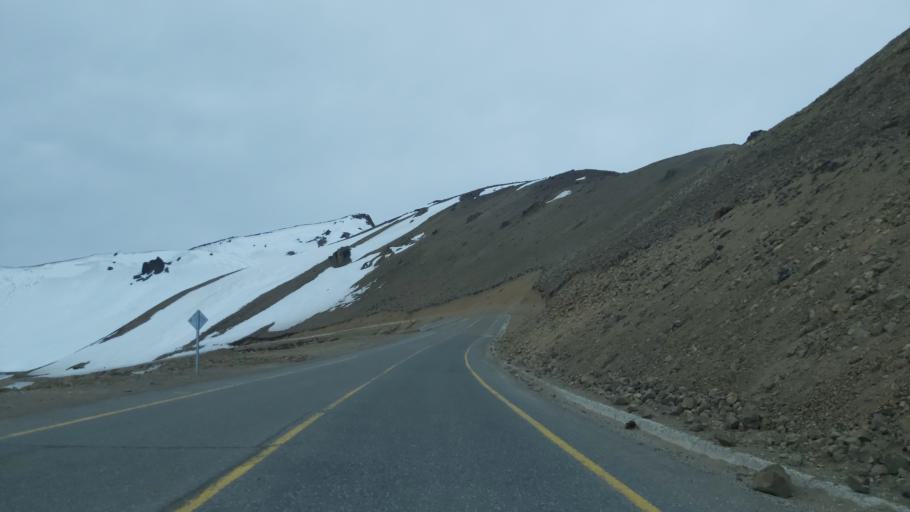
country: CL
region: Maule
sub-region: Provincia de Linares
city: Colbun
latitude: -36.0223
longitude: -70.5040
